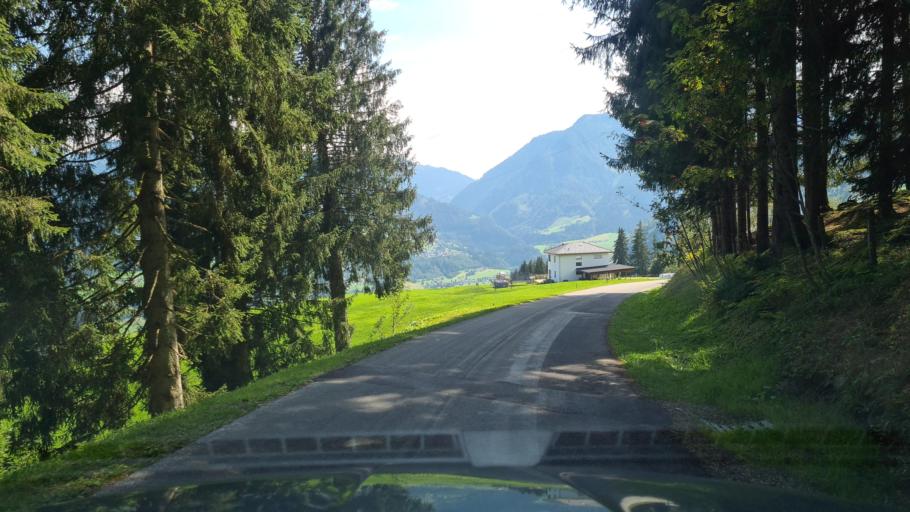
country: AT
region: Salzburg
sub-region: Politischer Bezirk Sankt Johann im Pongau
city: Sankt Johann im Pongau
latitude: 47.3579
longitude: 13.1802
